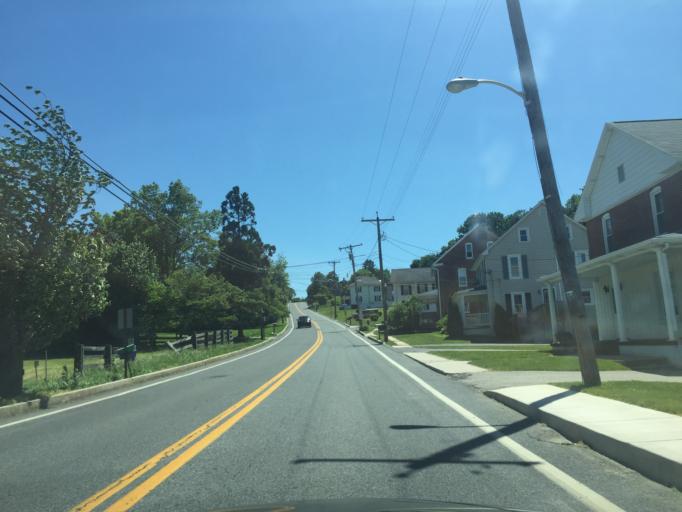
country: US
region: Maryland
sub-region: Carroll County
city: Manchester
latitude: 39.6596
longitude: -76.8871
